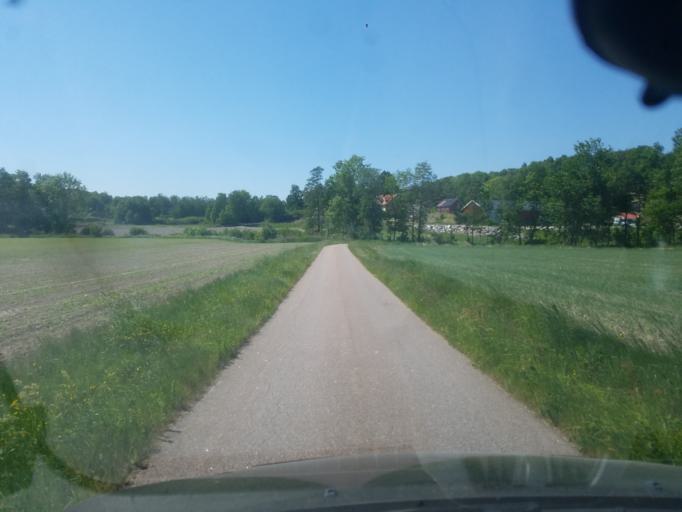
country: SE
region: Vaestra Goetaland
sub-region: Orust
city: Henan
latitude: 58.2647
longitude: 11.5724
